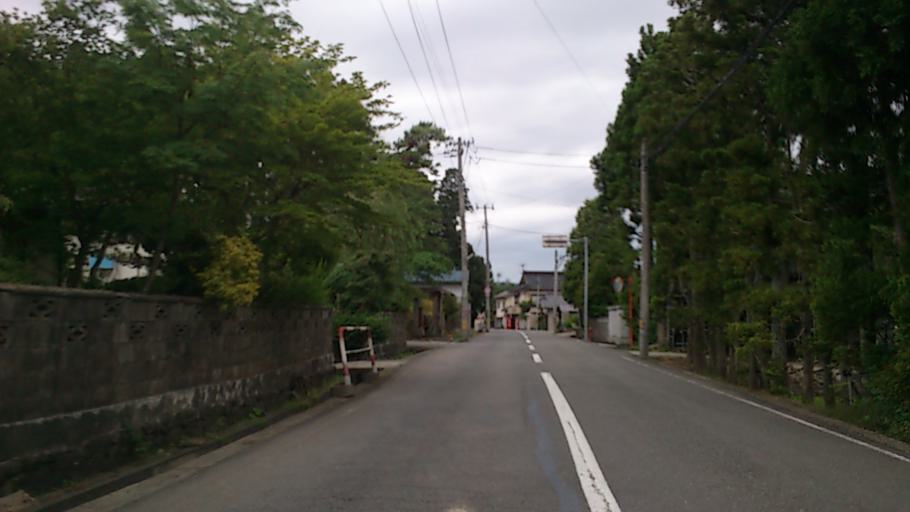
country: JP
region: Yamagata
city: Tsuruoka
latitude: 38.7427
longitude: 139.9633
